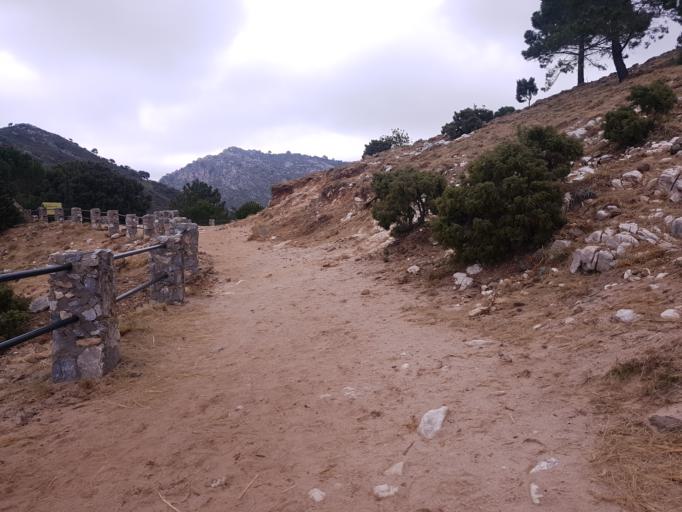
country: ES
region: Andalusia
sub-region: Provincia de Malaga
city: Ojen
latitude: 36.5655
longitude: -4.8910
